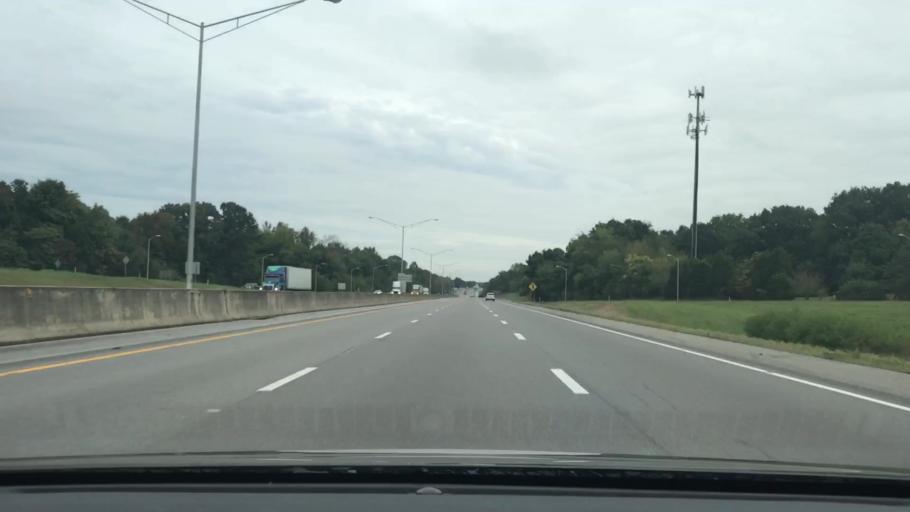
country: US
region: Kentucky
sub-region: Warren County
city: Bowling Green
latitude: 36.9784
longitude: -86.3904
